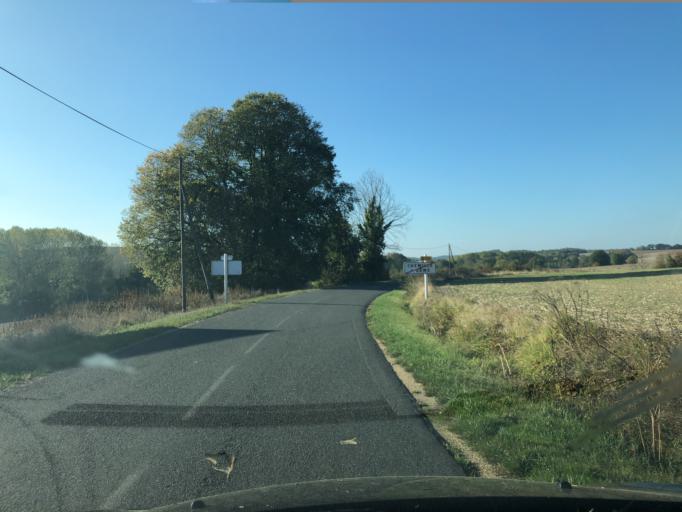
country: FR
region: Centre
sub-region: Departement d'Indre-et-Loire
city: Neuvy-le-Roi
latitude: 47.6591
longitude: 0.6416
